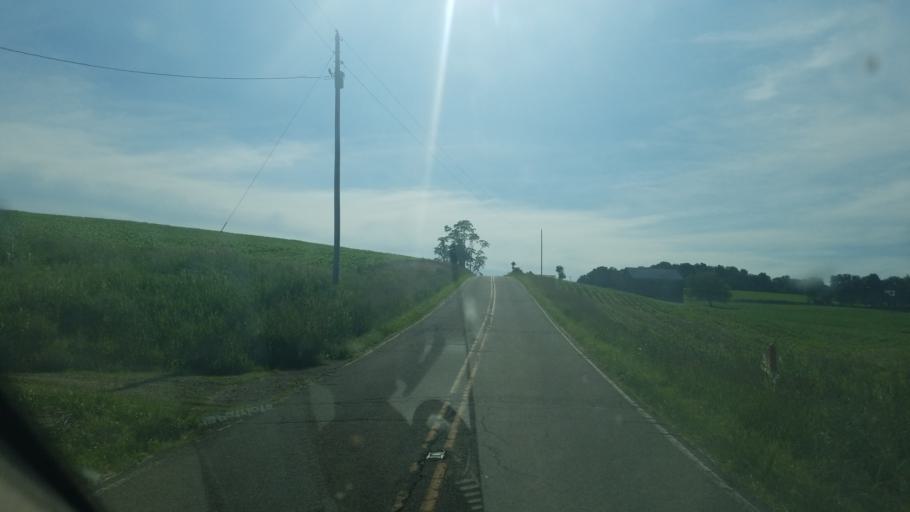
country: US
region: Ohio
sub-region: Holmes County
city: Millersburg
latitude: 40.4397
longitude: -81.9430
